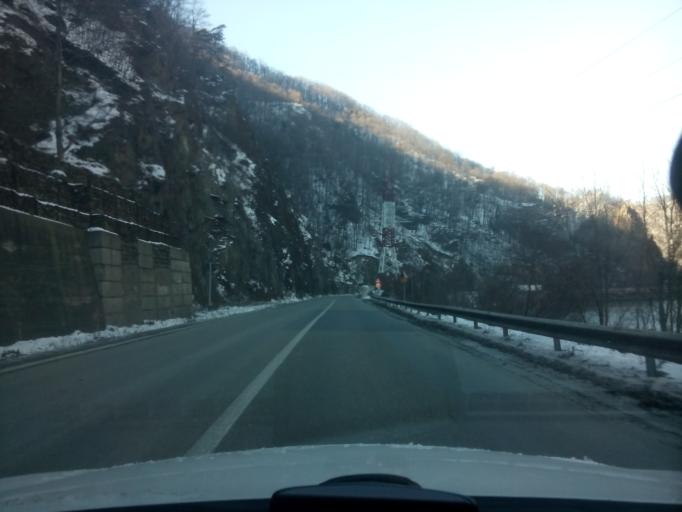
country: RO
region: Valcea
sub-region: Comuna Brezoi
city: Brezoi
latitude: 45.2937
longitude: 24.2923
